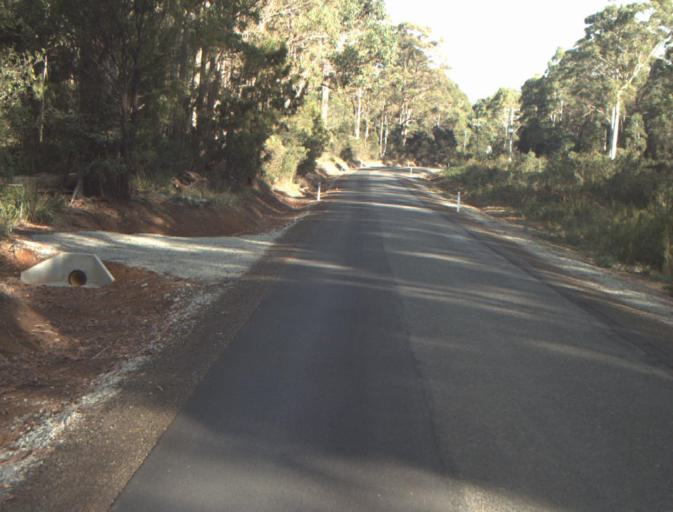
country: AU
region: Tasmania
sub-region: Launceston
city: Mayfield
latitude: -41.3062
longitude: 147.1989
